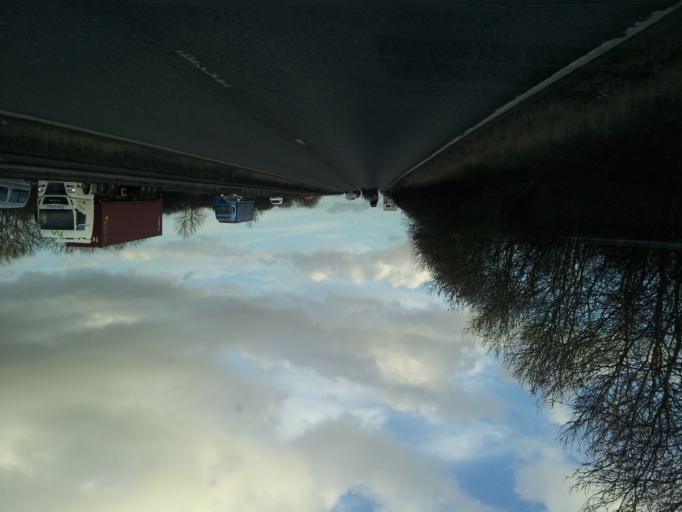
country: GB
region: England
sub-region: District of Rutland
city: Clipsham
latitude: 52.7963
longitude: -0.6108
